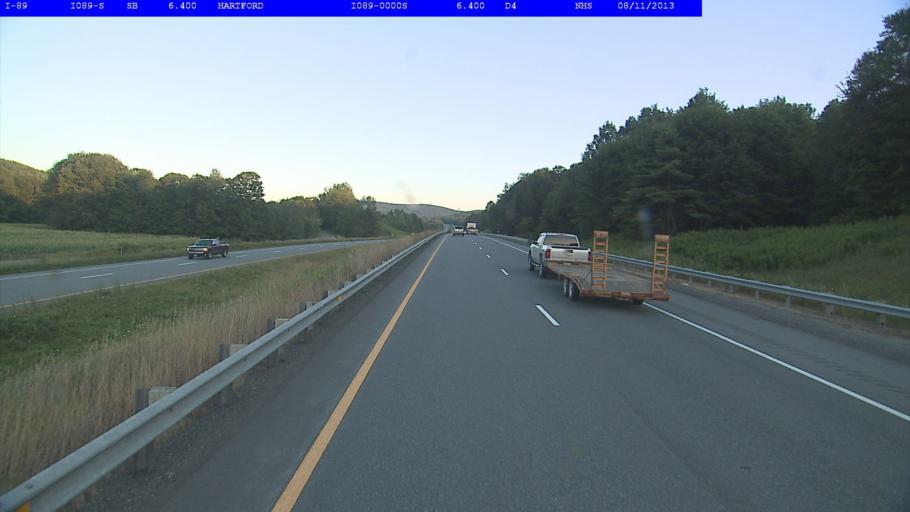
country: US
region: Vermont
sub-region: Windsor County
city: White River Junction
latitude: 43.6977
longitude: -72.4089
